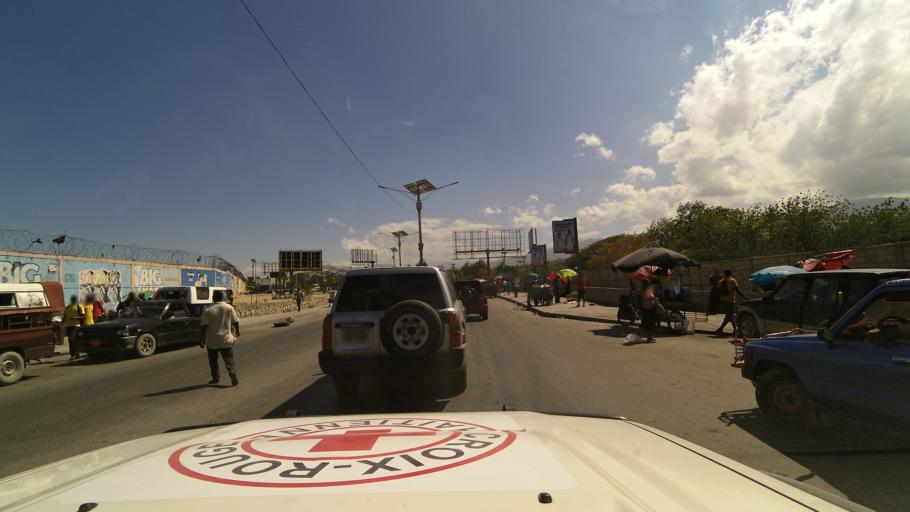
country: HT
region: Ouest
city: Delmas 73
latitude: 18.5759
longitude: -72.3063
